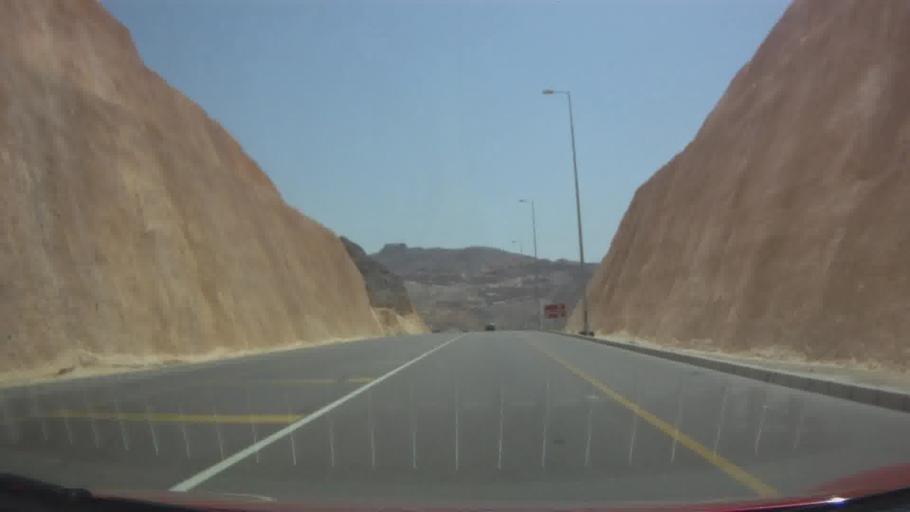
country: OM
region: Muhafazat Masqat
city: Muscat
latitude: 23.5394
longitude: 58.6481
